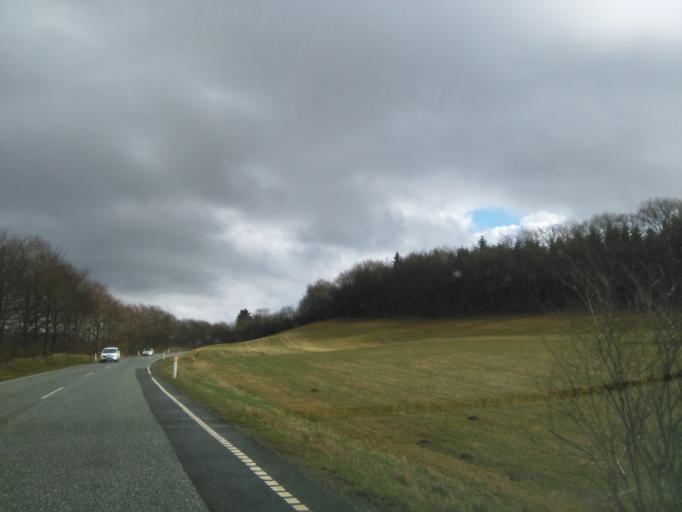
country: DK
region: Central Jutland
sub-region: Silkeborg Kommune
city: Svejbaek
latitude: 56.0913
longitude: 9.6723
